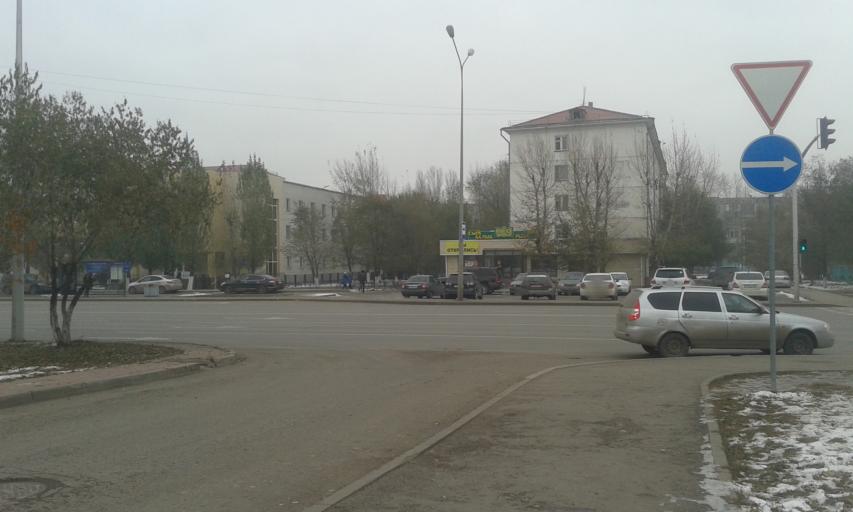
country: KZ
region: Astana Qalasy
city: Astana
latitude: 51.1548
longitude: 71.4784
